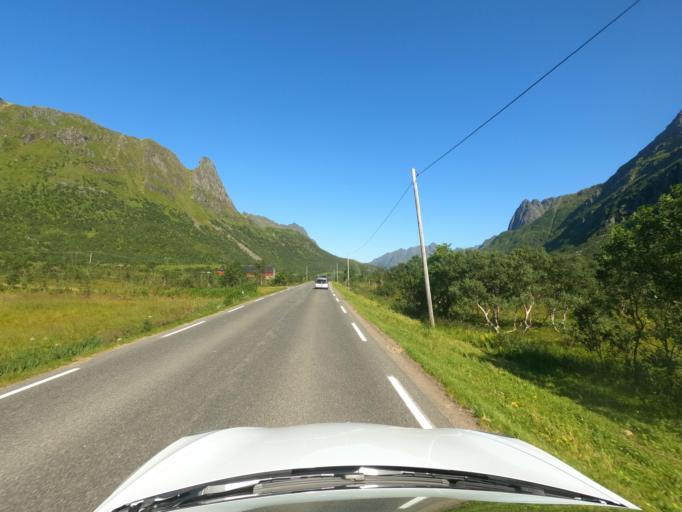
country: NO
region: Nordland
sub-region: Hadsel
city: Melbu
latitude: 68.3622
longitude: 14.7572
